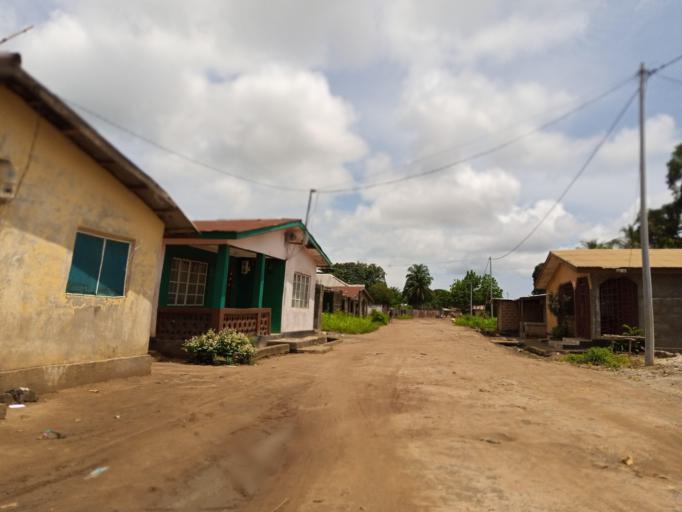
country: SL
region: Northern Province
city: Masoyila
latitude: 8.6028
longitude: -13.1827
